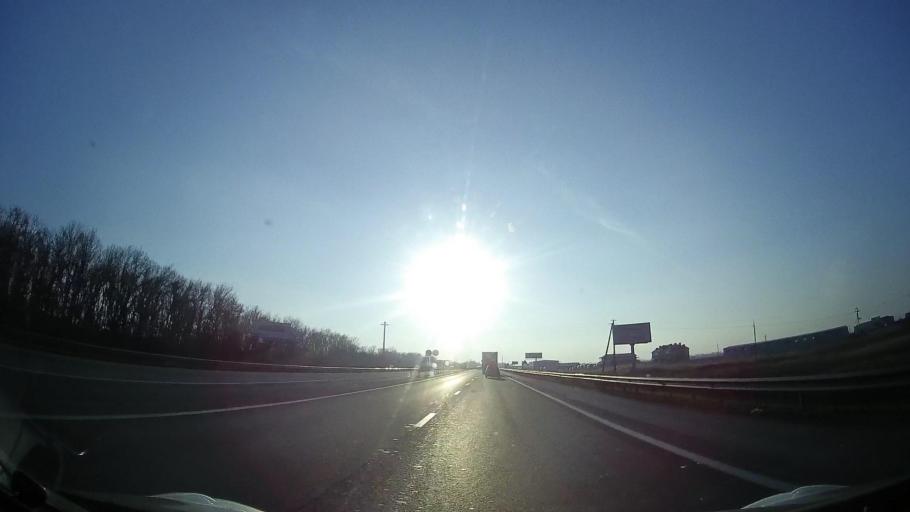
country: RU
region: Rostov
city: Ol'ginskaya
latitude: 47.1245
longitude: 39.8705
